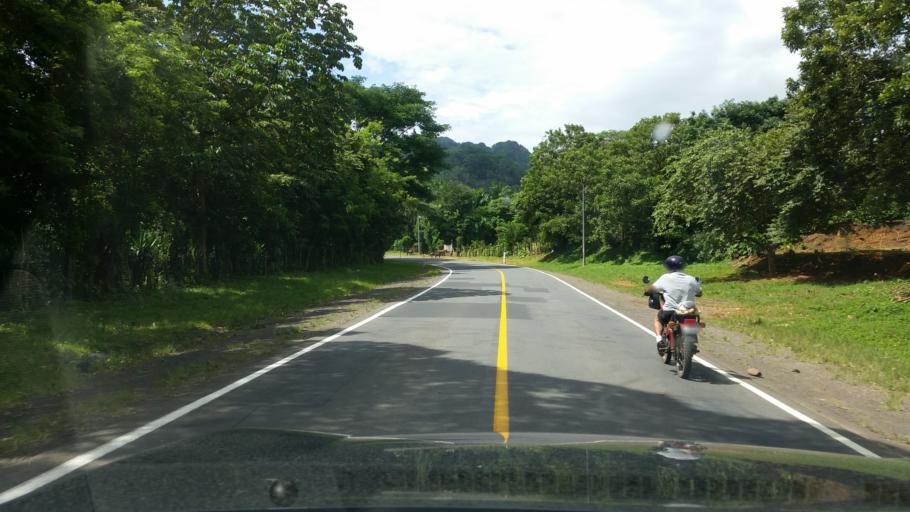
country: NI
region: Matagalpa
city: San Ramon
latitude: 12.9491
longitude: -85.8716
